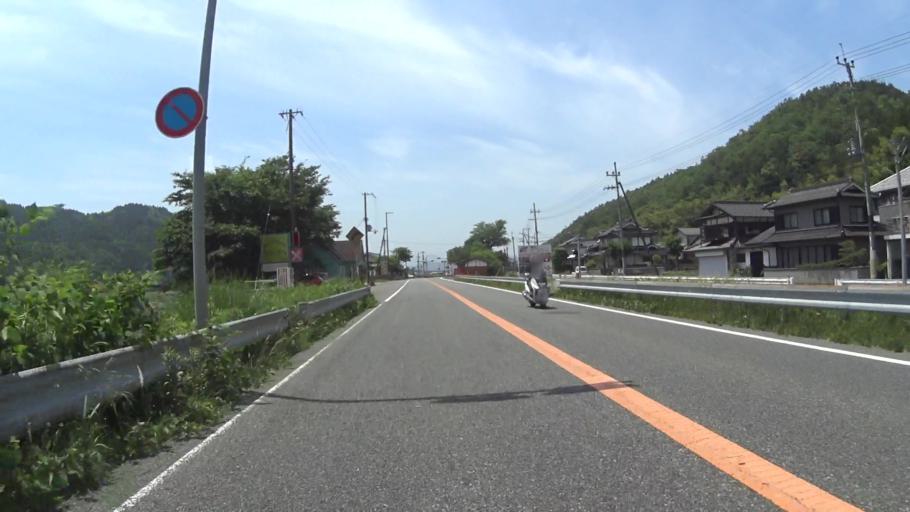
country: JP
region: Kyoto
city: Ayabe
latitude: 35.2576
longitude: 135.1989
